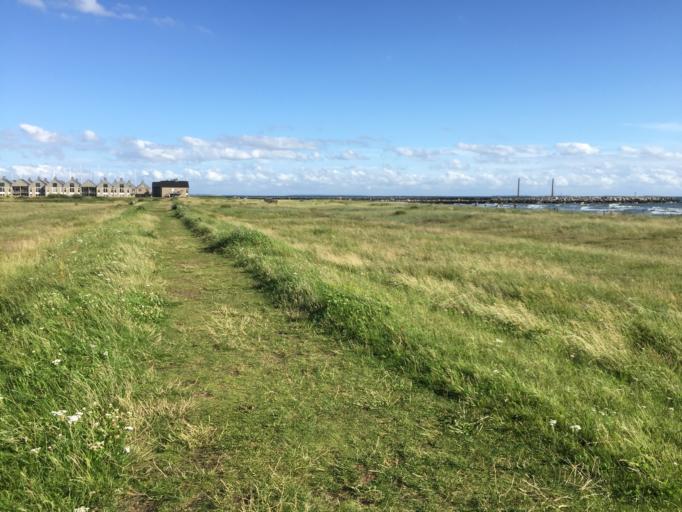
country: DK
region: Zealand
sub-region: Naestved Kommune
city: Naestved
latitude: 55.1788
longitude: 11.6372
